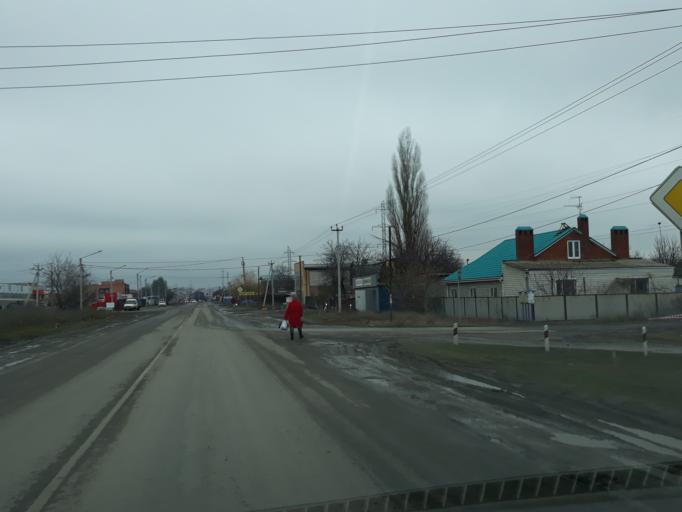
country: RU
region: Rostov
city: Novobessergenovka
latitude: 47.2230
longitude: 38.8406
